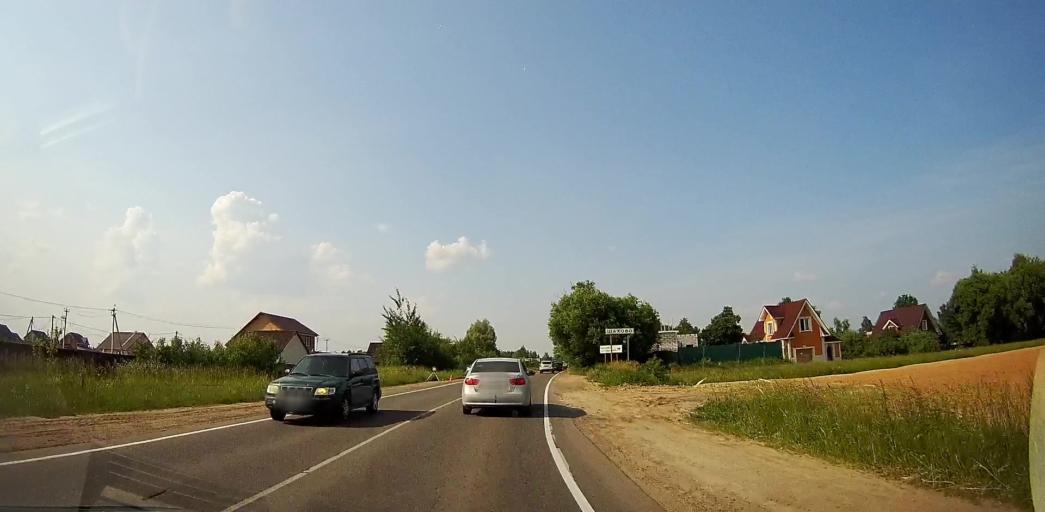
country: RU
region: Moskovskaya
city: Zhitnevo
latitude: 55.3132
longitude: 37.9005
